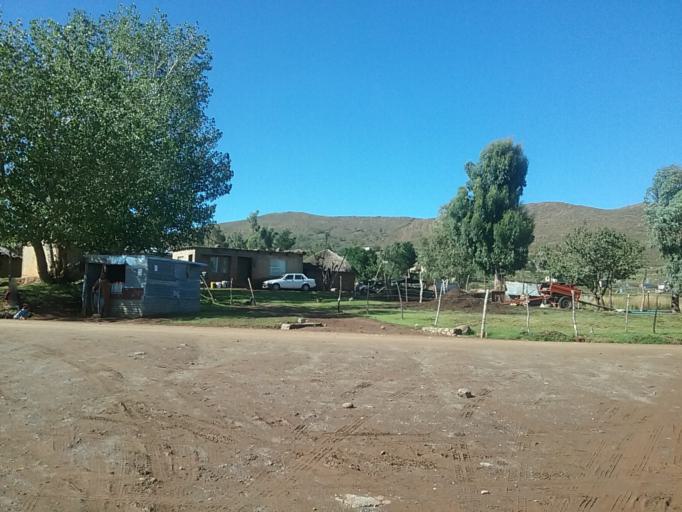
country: LS
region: Berea
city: Teyateyaneng
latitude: -29.2284
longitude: 27.8670
